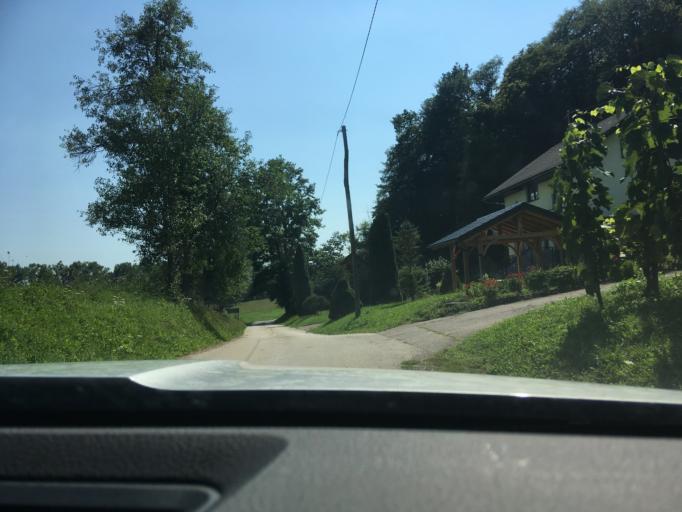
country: SI
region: Metlika
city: Metlika
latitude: 45.6095
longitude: 15.2807
